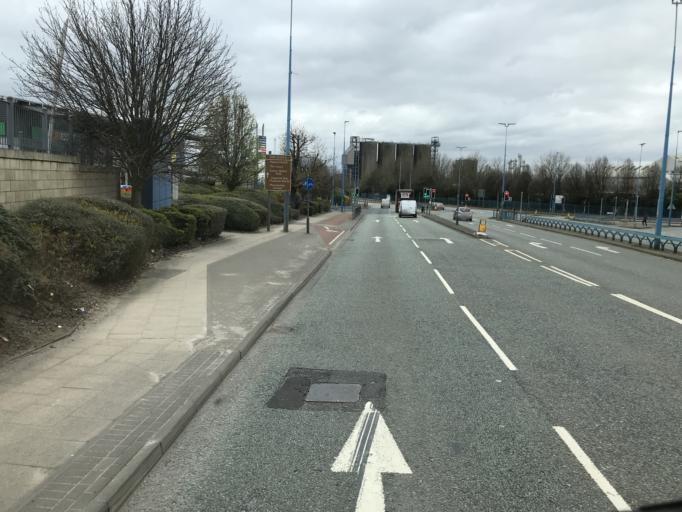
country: GB
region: England
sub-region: City and Borough of Salford
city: Eccles
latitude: 53.4829
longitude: -2.3305
